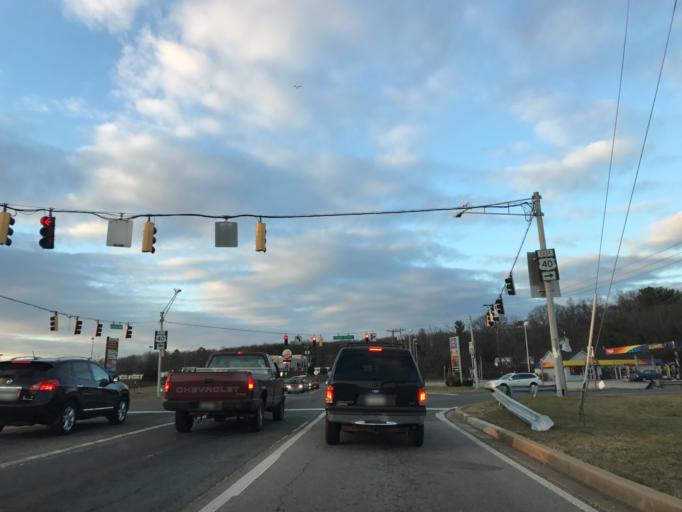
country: US
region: Maryland
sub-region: Cecil County
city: North East
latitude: 39.6082
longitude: -75.9477
